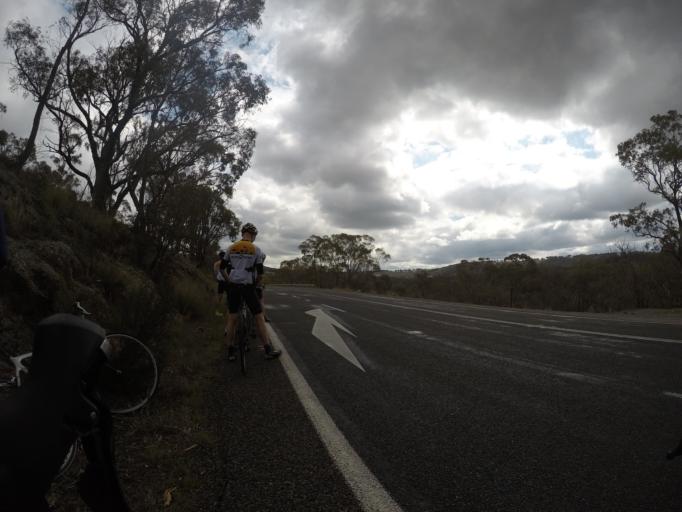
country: AU
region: New South Wales
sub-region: Bathurst Regional
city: Eglinton
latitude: -33.4243
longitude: 149.4327
